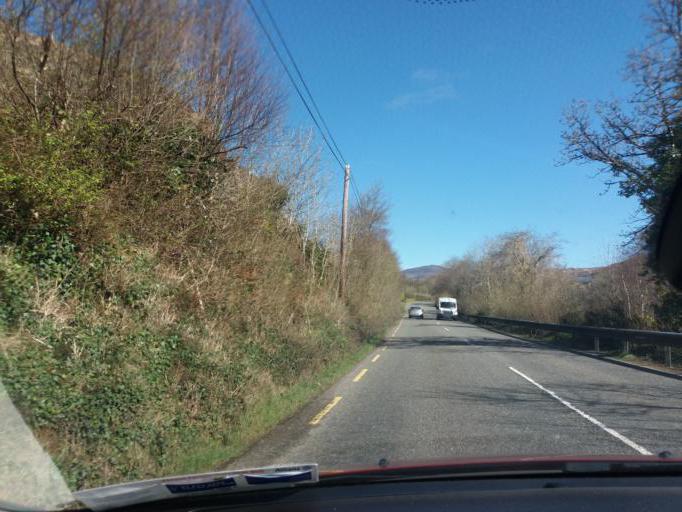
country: IE
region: Munster
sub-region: Ciarrai
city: Cill Airne
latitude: 51.9240
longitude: -9.3844
